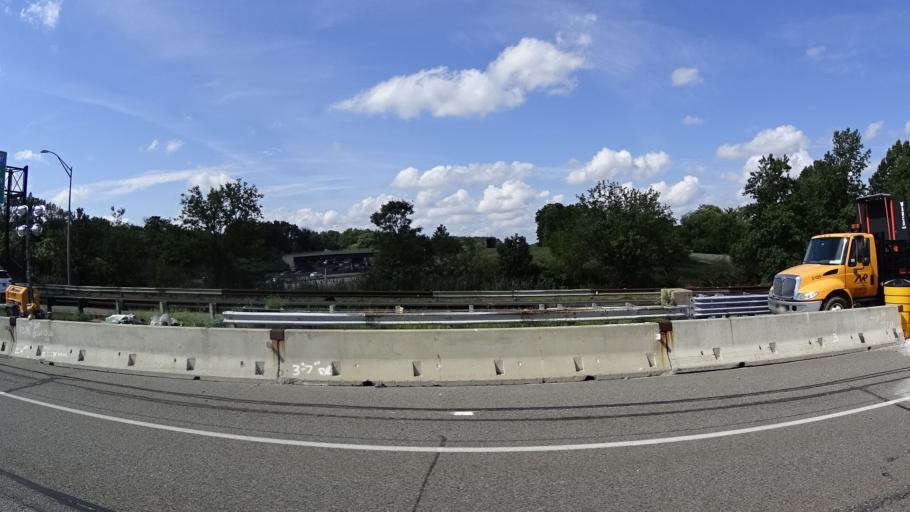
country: US
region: New Jersey
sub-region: Middlesex County
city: Fords
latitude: 40.5421
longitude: -74.3094
